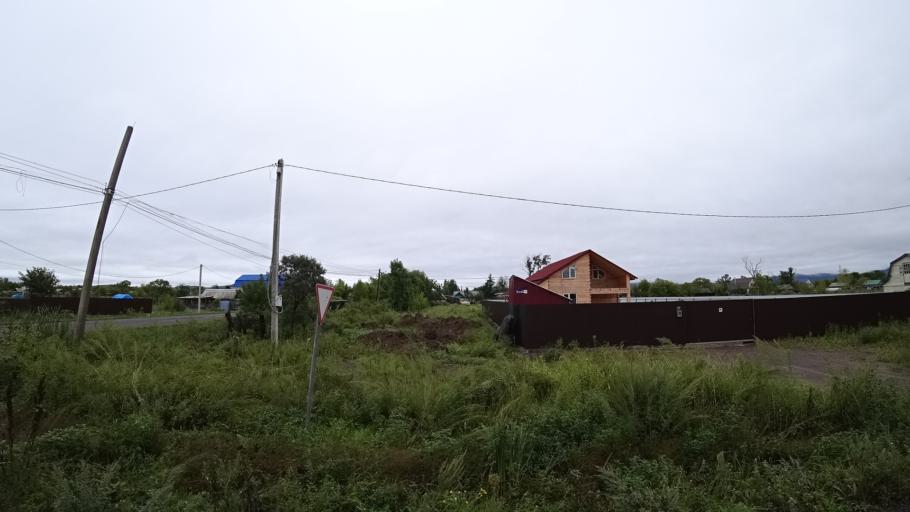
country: RU
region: Primorskiy
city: Monastyrishche
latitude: 44.1999
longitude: 132.4655
